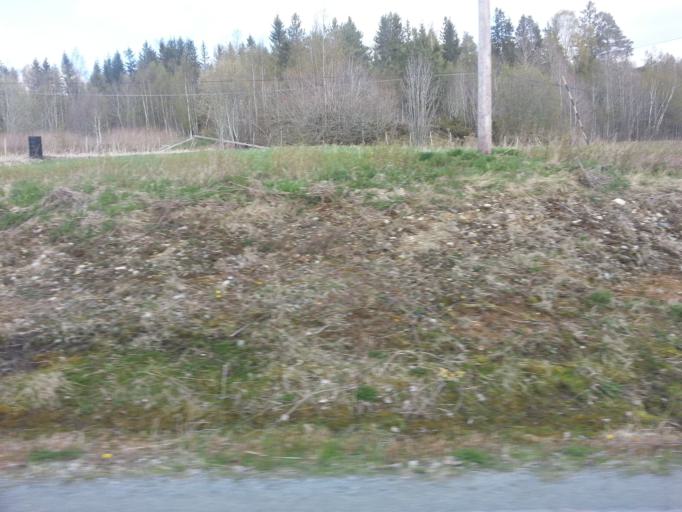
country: NO
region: Nord-Trondelag
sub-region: Levanger
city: Skogn
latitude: 63.6285
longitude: 11.1860
